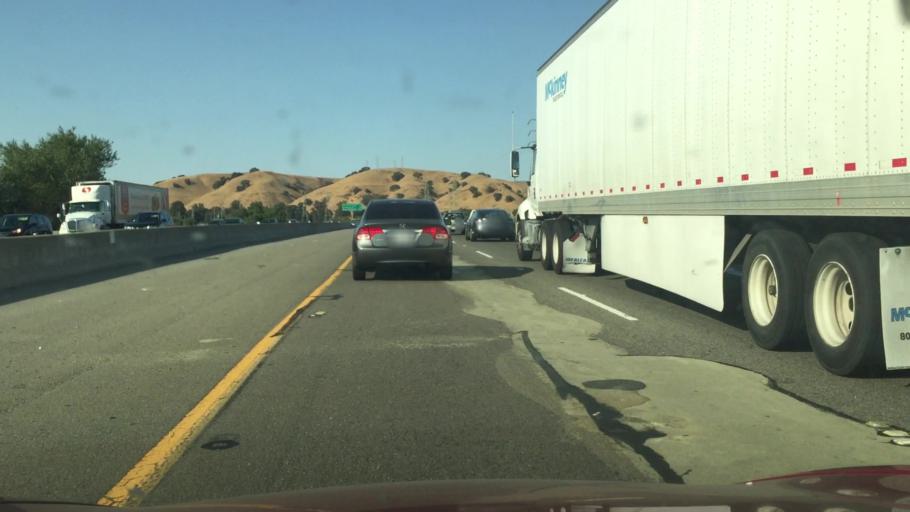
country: US
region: California
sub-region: Alameda County
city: Pleasanton
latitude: 37.5787
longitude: -121.8801
